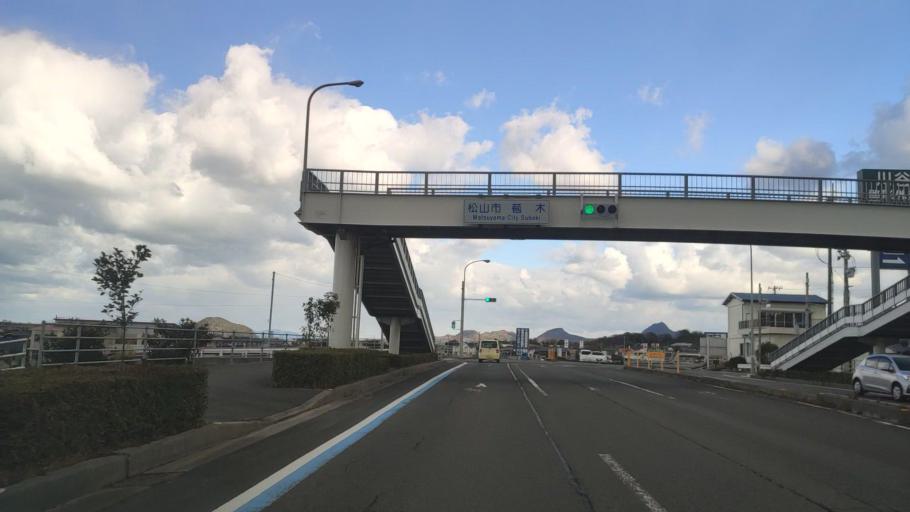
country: JP
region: Ehime
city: Hojo
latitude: 33.9395
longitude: 132.7737
